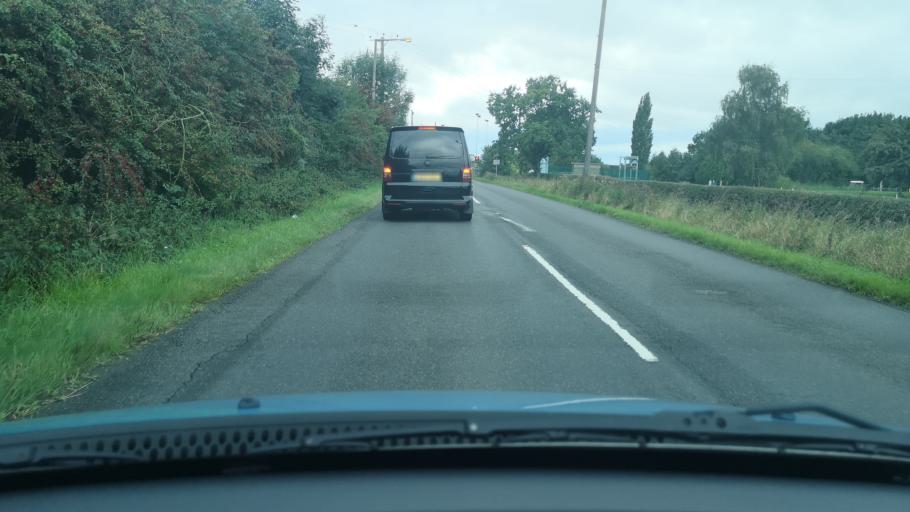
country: GB
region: England
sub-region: Doncaster
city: Hatfield
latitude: 53.6033
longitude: -0.9776
